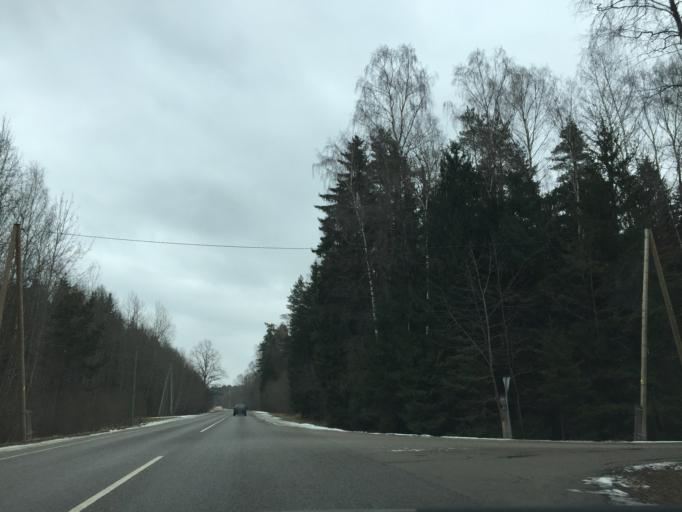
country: LV
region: Kegums
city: Kegums
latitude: 56.7556
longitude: 24.7383
